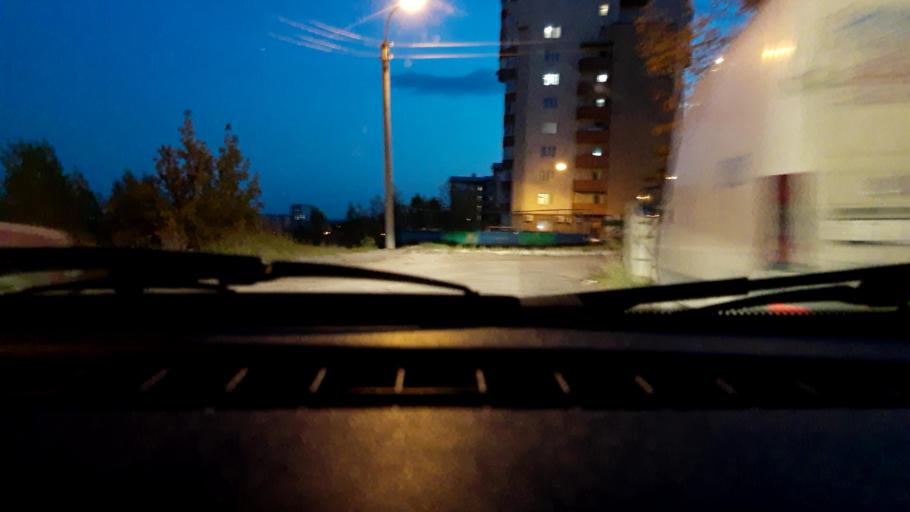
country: RU
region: Bashkortostan
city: Ufa
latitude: 54.7778
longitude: 56.0473
